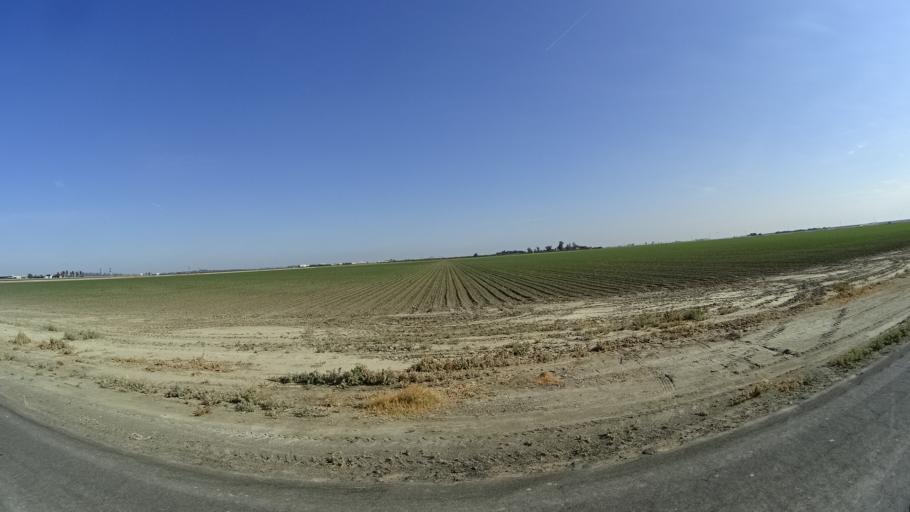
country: US
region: California
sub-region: Kings County
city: Home Garden
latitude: 36.2258
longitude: -119.6430
